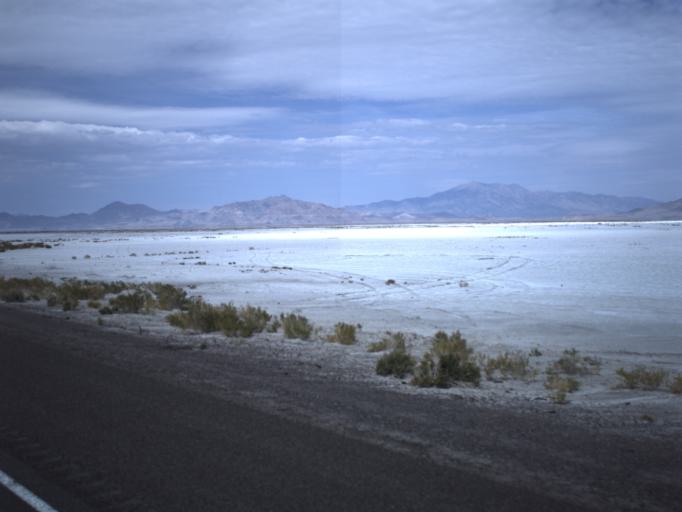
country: US
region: Utah
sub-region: Tooele County
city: Wendover
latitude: 40.7368
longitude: -113.7252
